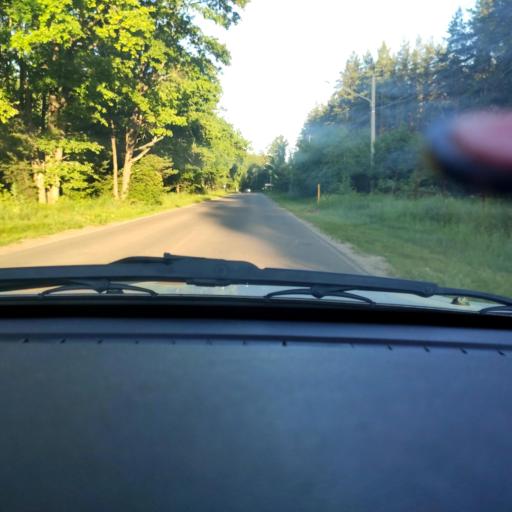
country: RU
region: Voronezj
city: Ramon'
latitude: 51.8948
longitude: 39.2784
